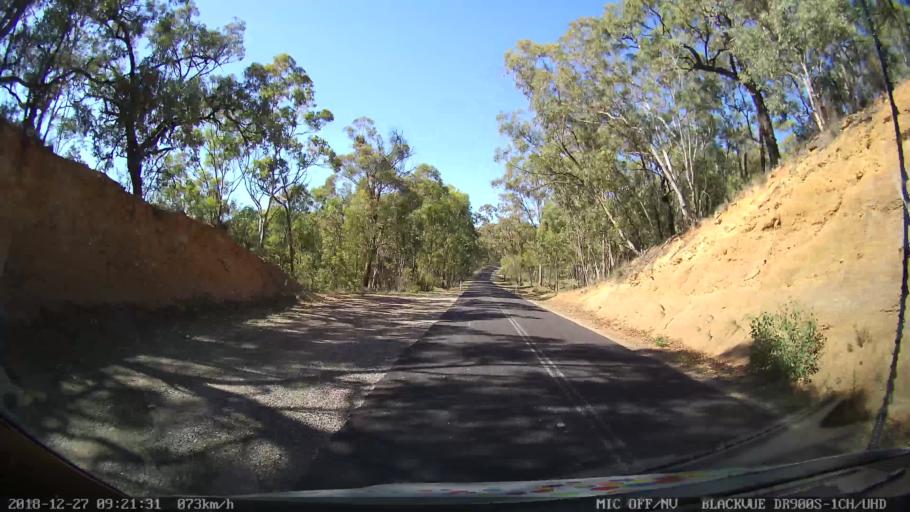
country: AU
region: New South Wales
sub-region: Lithgow
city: Portland
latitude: -33.1246
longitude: 150.0160
